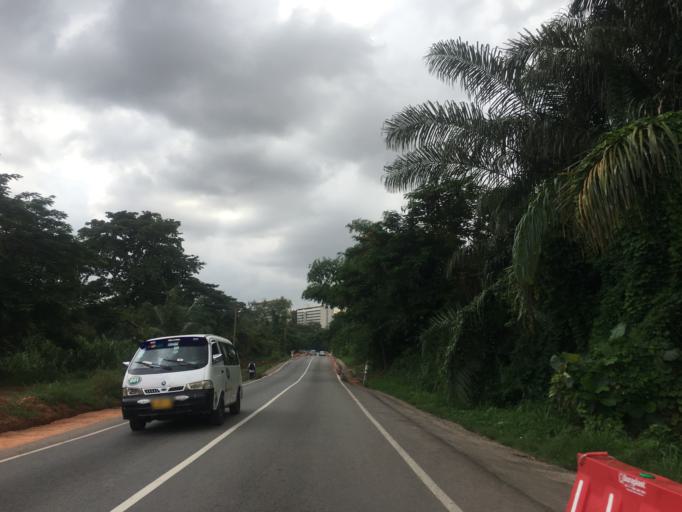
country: GH
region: Ashanti
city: Kumasi
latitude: 6.6774
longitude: -1.5674
